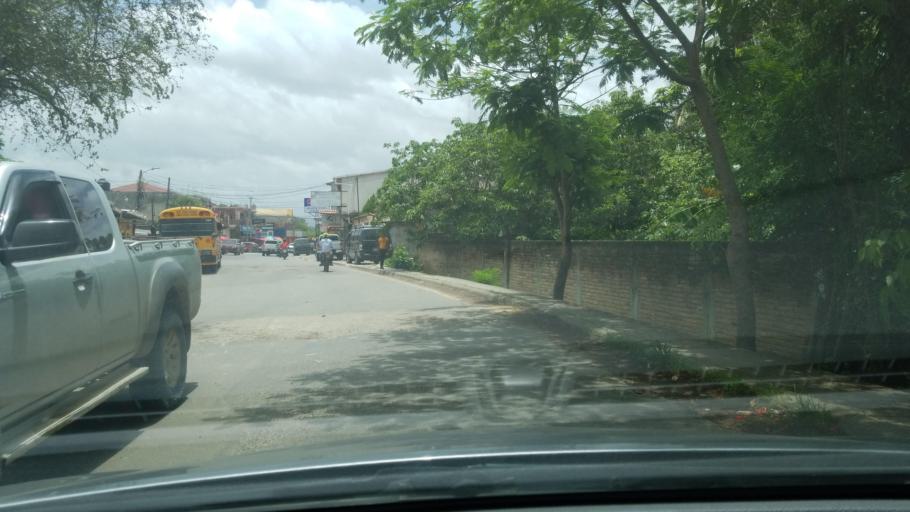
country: HN
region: Copan
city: Cucuyagua
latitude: 14.6497
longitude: -88.8762
